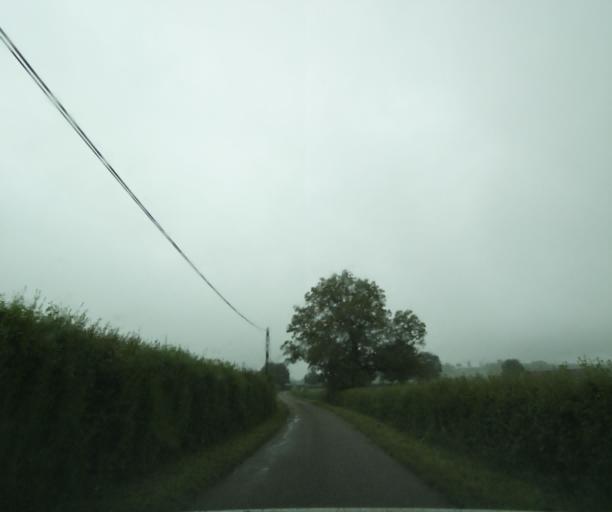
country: FR
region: Bourgogne
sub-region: Departement de Saone-et-Loire
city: Charolles
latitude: 46.4266
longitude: 4.3468
